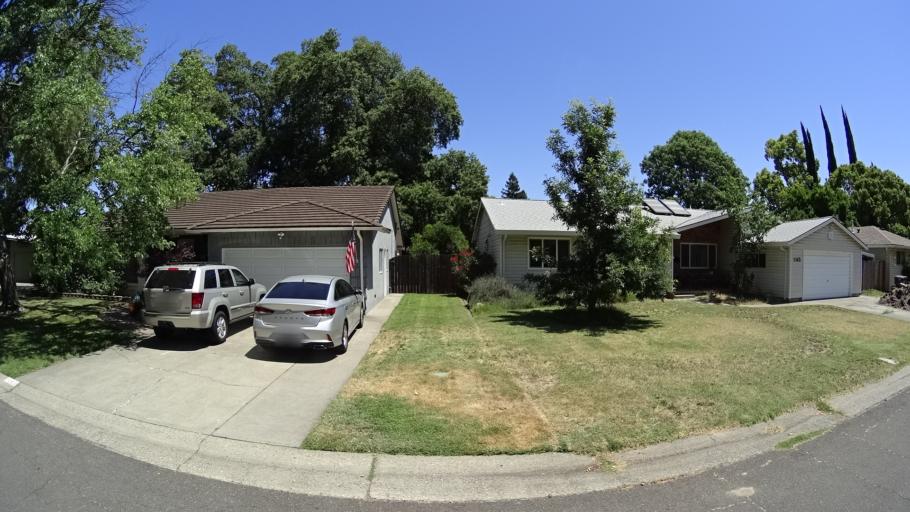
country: US
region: California
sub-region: Yolo County
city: West Sacramento
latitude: 38.5342
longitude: -121.5138
